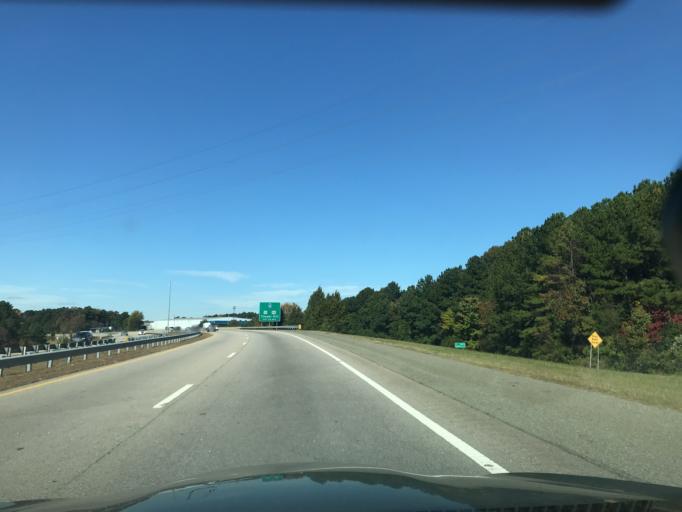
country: US
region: North Carolina
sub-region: Durham County
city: Durham
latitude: 36.0121
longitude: -78.9345
